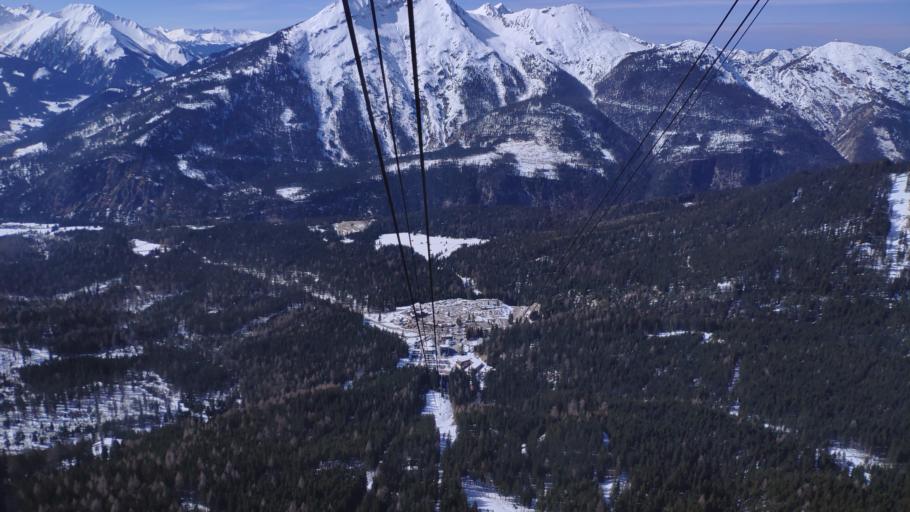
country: AT
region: Tyrol
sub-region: Politischer Bezirk Reutte
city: Ehrwald
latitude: 47.4247
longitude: 10.9578
